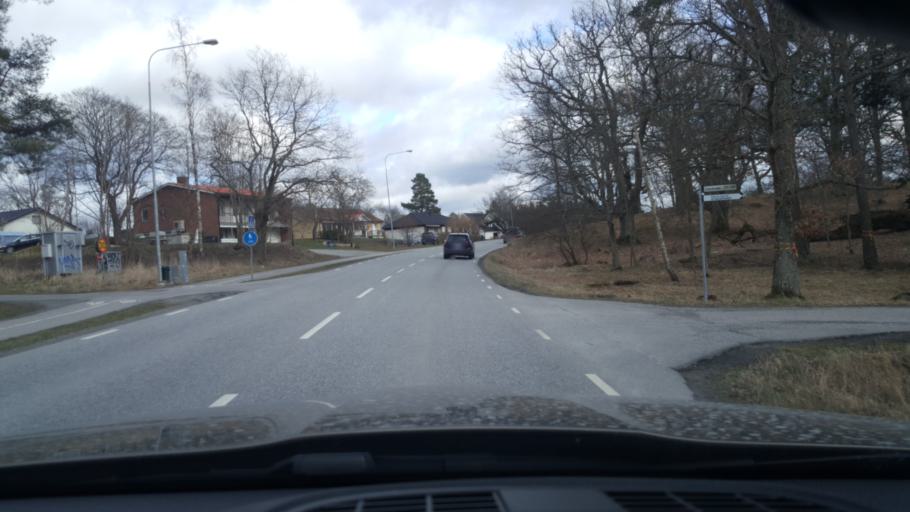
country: SE
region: Stockholm
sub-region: Osterakers Kommun
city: Akersberga
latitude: 59.4923
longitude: 18.2848
